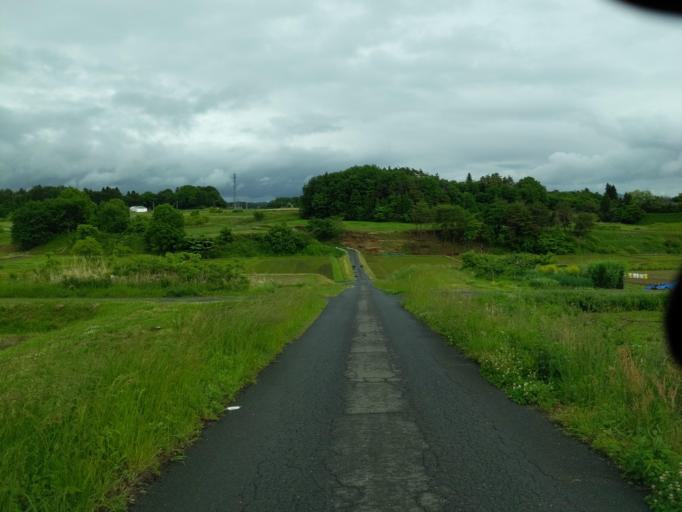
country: JP
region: Fukushima
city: Koriyama
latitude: 37.3595
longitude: 140.4106
